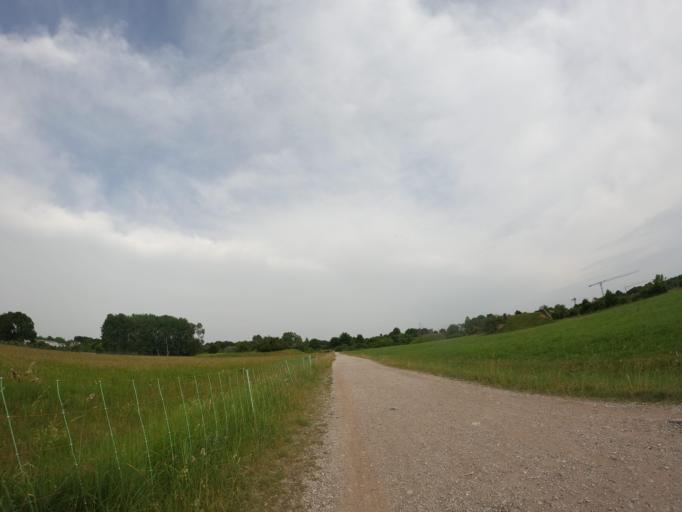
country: DE
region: Bavaria
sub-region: Upper Bavaria
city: Neubiberg
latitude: 48.0676
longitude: 11.6470
